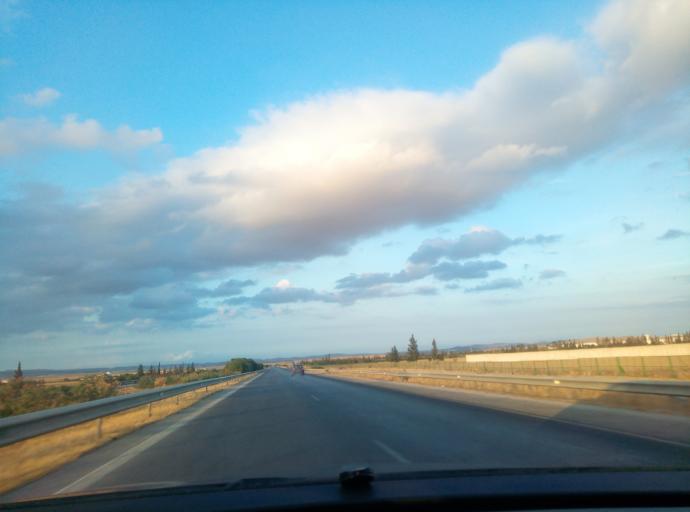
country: TN
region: Manouba
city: El Battan
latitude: 36.6890
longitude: 9.9251
